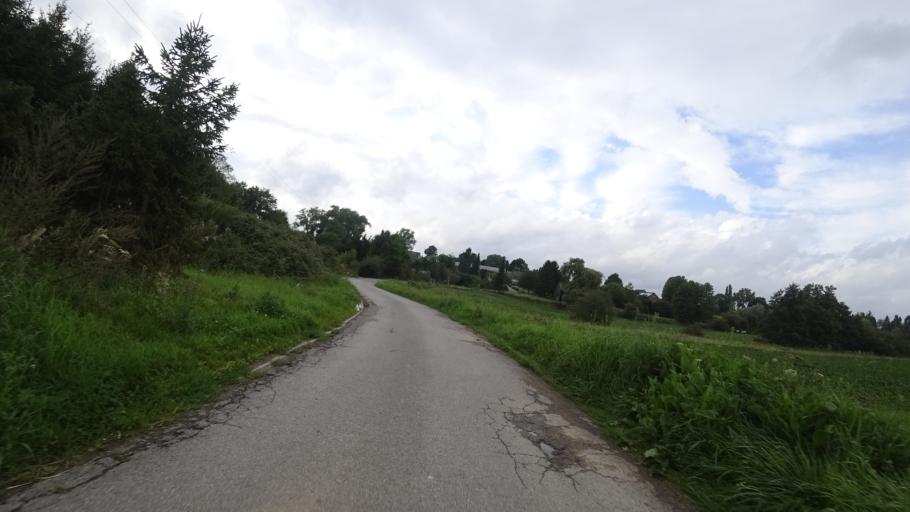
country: BE
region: Wallonia
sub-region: Province de Namur
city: Gembloux
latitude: 50.5565
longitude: 4.7429
